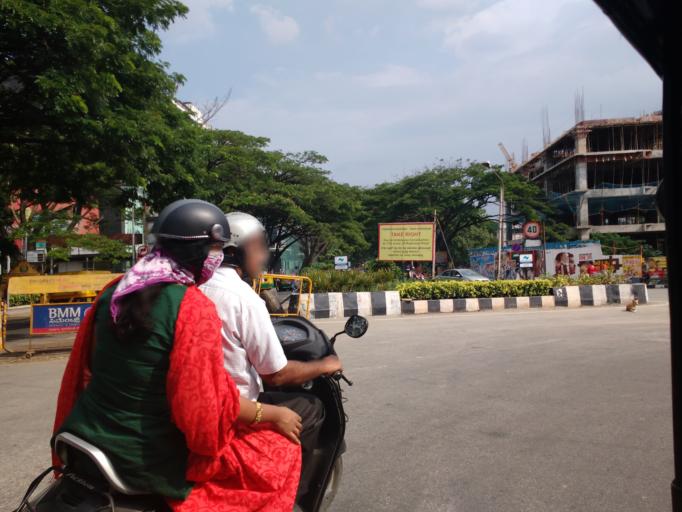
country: IN
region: Karnataka
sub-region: Bangalore Urban
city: Bangalore
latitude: 13.0125
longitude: 77.5544
